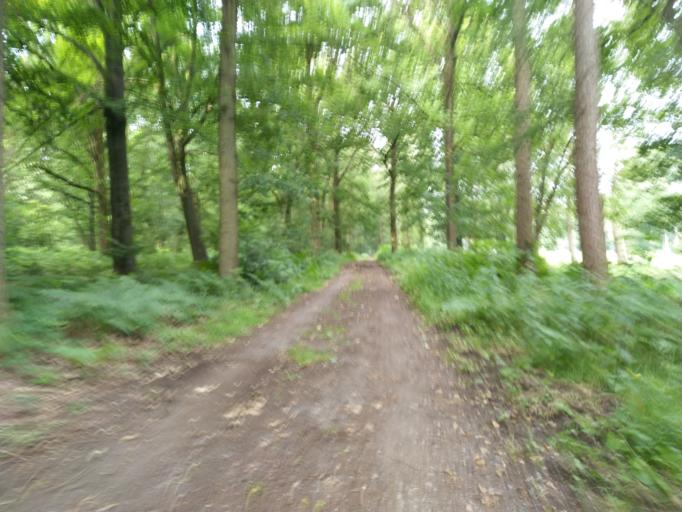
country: BE
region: Wallonia
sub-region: Province du Hainaut
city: Saint-Ghislain
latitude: 50.5003
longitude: 3.8190
